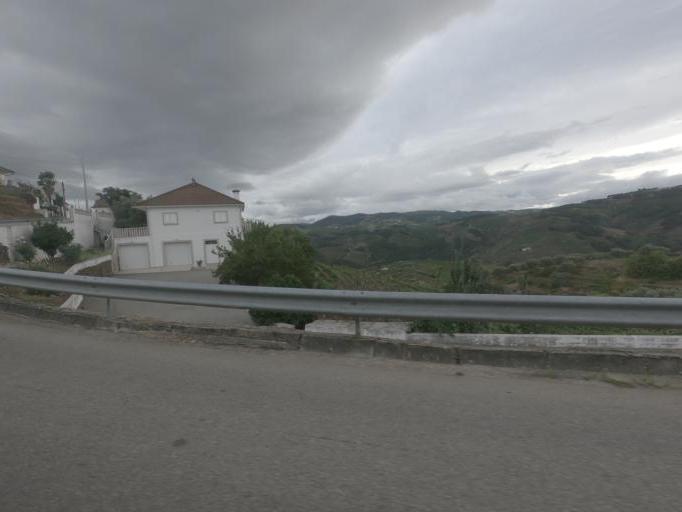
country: PT
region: Vila Real
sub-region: Sabrosa
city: Sabrosa
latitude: 41.2802
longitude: -7.5376
